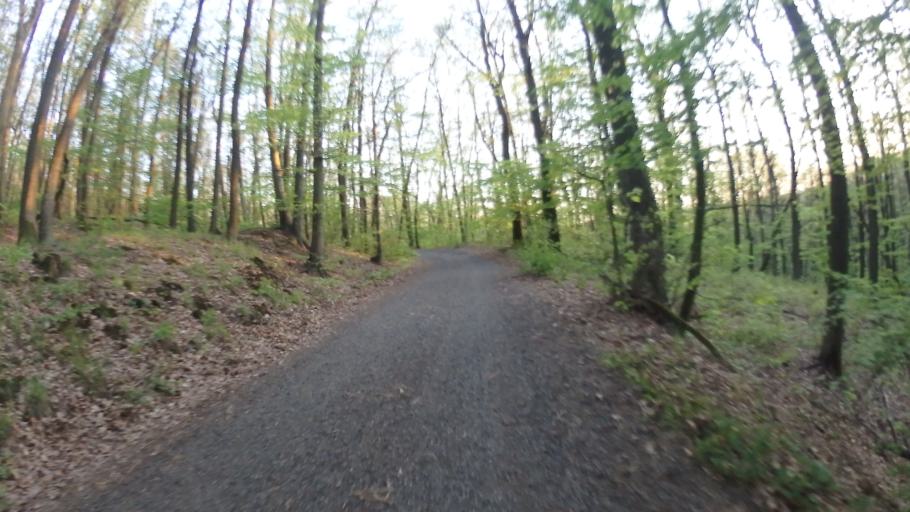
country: CZ
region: South Moravian
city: Troubsko
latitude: 49.1929
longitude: 16.5150
